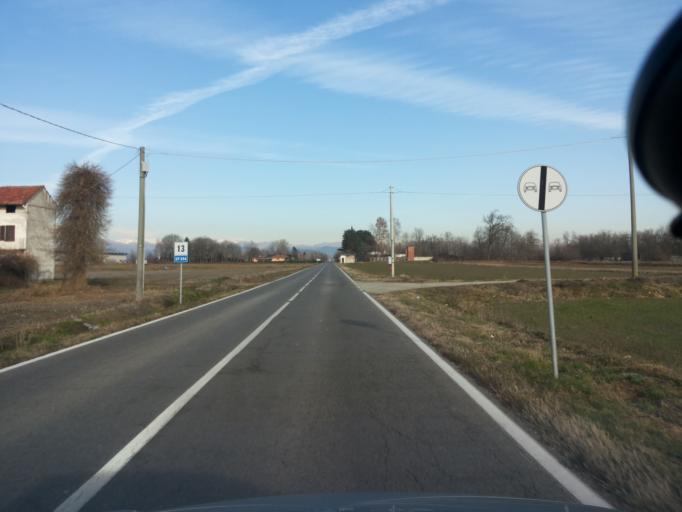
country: IT
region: Piedmont
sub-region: Provincia di Vercelli
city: Arborio
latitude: 45.5052
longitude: 8.3887
